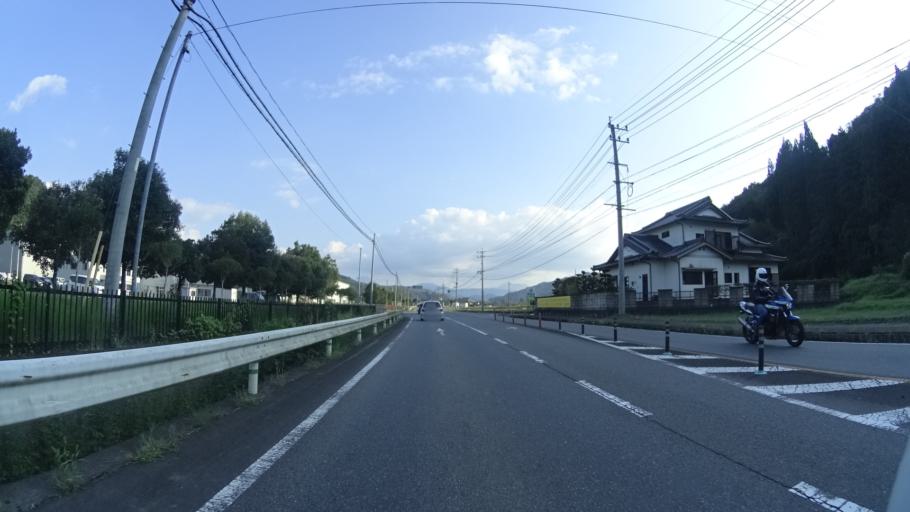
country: JP
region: Oita
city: Bungo-Takada-shi
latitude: 33.4692
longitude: 131.3278
